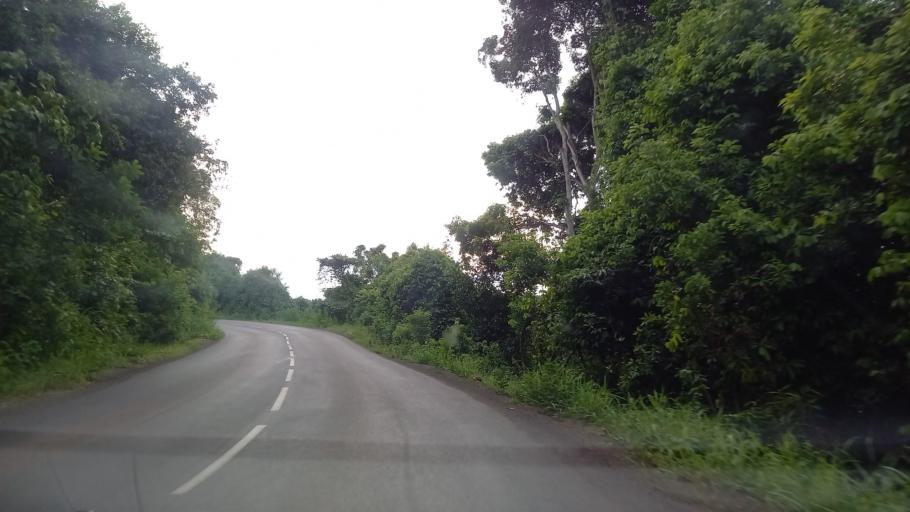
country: YT
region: Bandraboua
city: Bandraboua
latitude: -12.7360
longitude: 45.1191
